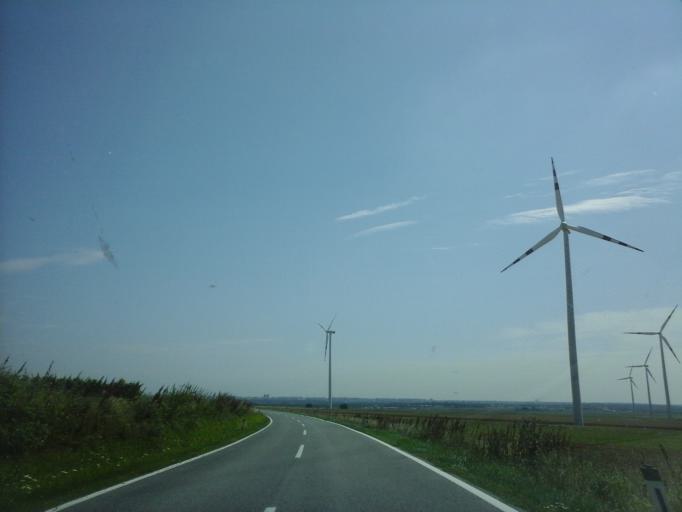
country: AT
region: Lower Austria
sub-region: Politischer Bezirk Bruck an der Leitha
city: Berg
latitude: 48.0950
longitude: 17.0126
